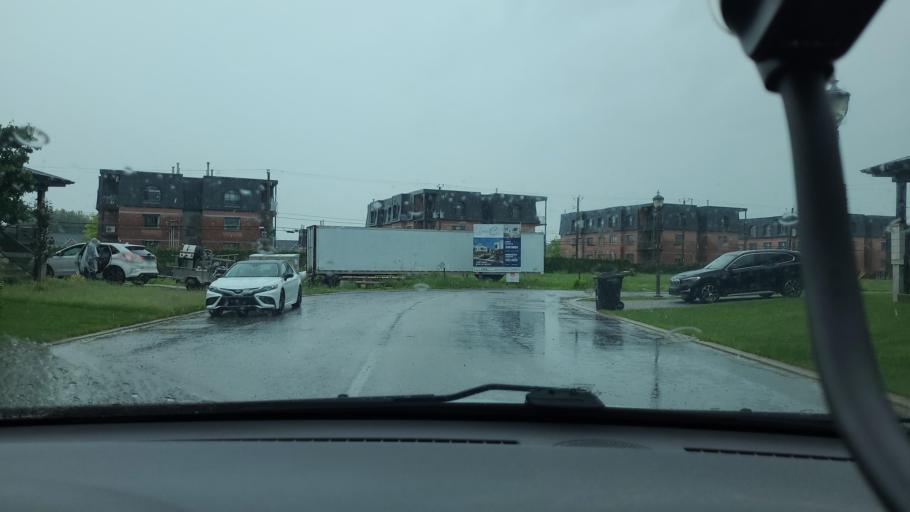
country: CA
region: Quebec
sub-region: Monteregie
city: Saint-Hyacinthe
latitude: 45.6112
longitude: -72.9863
